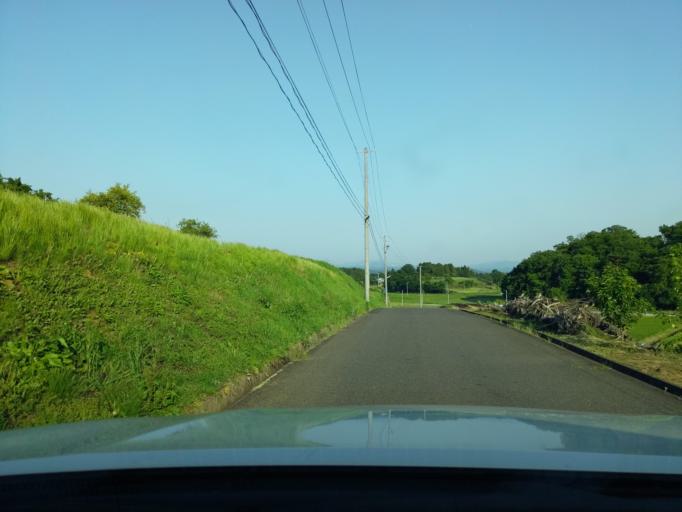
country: JP
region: Fukushima
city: Motomiya
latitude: 37.5368
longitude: 140.3549
